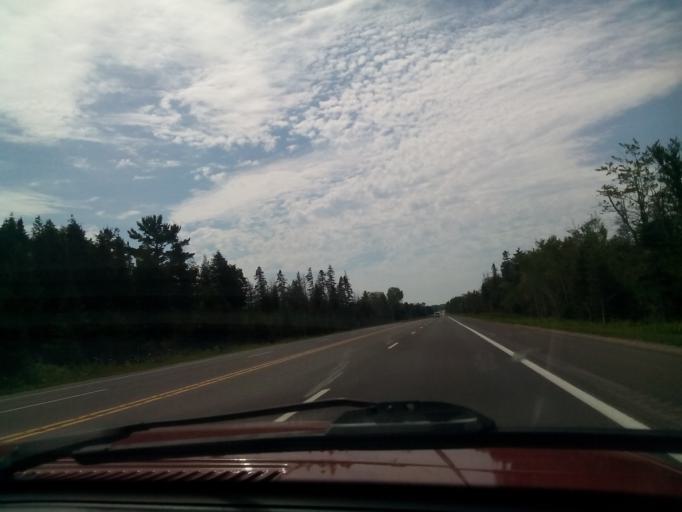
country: US
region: Michigan
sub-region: Schoolcraft County
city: Manistique
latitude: 46.0095
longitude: -85.9961
